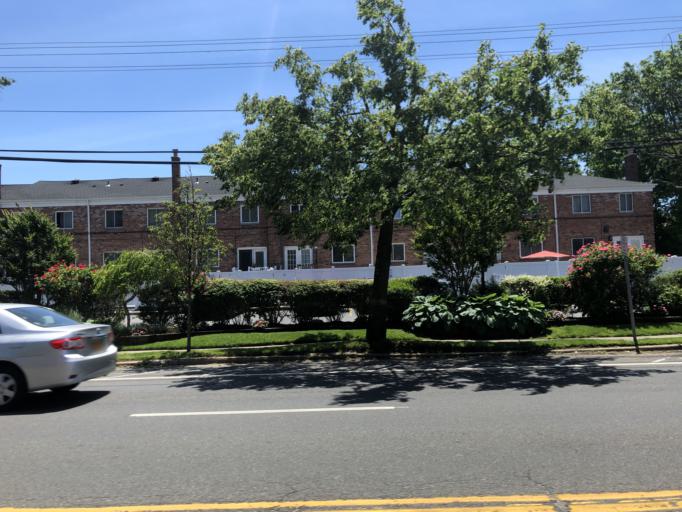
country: US
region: New York
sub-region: Nassau County
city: Baldwin
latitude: 40.6512
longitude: -73.6082
